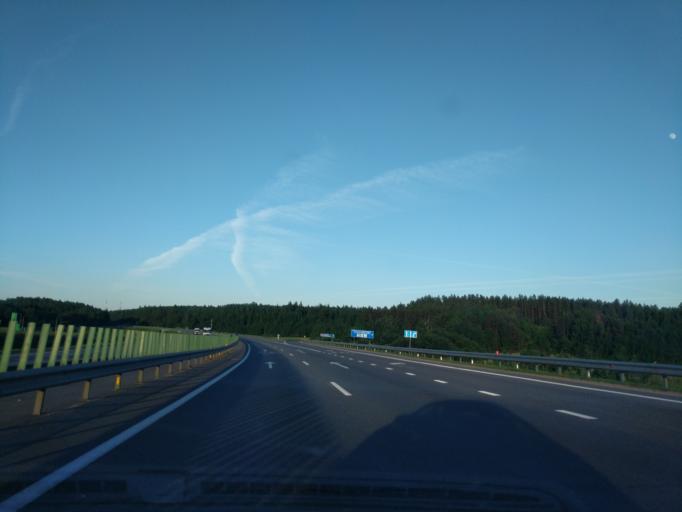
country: BY
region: Minsk
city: Novosel'ye
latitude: 53.9128
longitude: 27.2495
